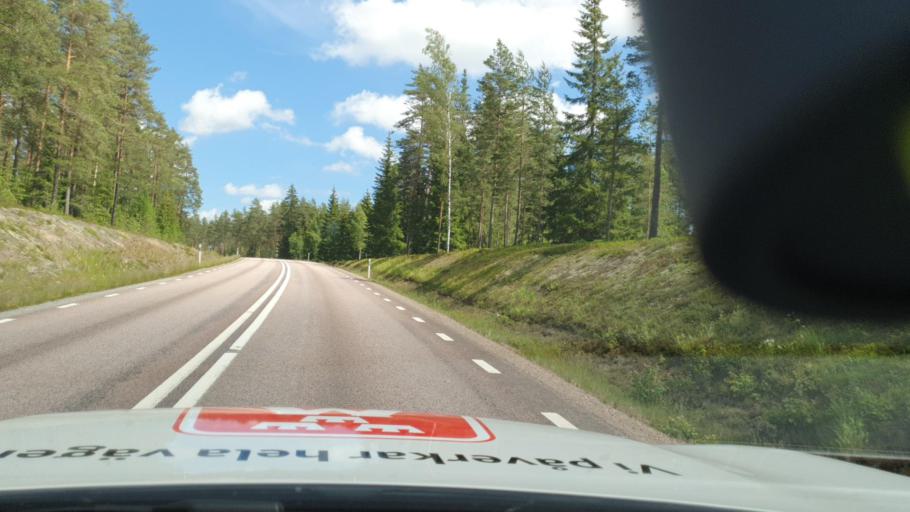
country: SE
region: Vaermland
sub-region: Karlstads Kommun
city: Molkom
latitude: 59.6204
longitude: 13.9397
